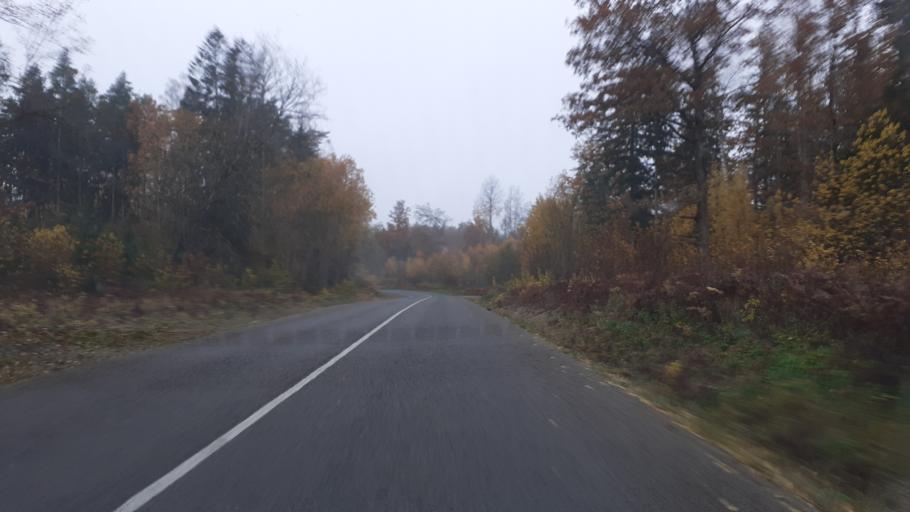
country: LV
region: Kuldigas Rajons
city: Kuldiga
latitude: 56.9550
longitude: 21.8791
